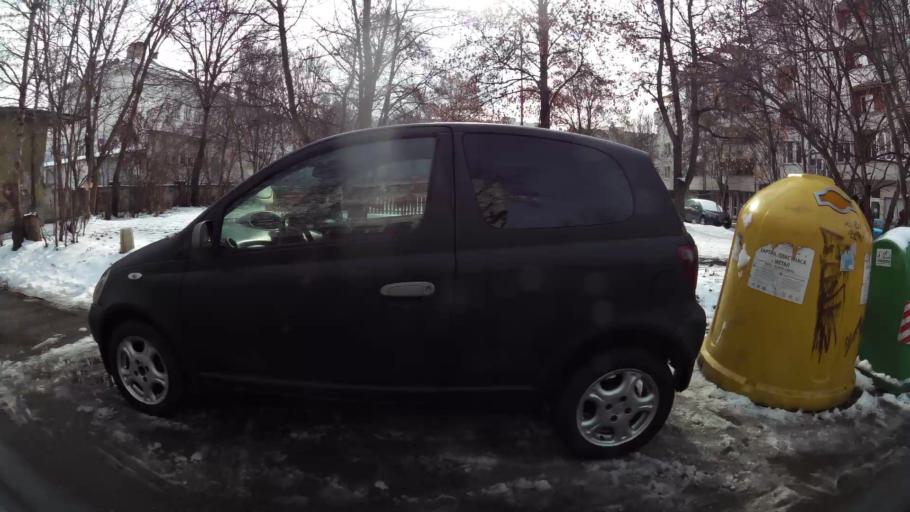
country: BG
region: Sofia-Capital
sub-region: Stolichna Obshtina
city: Sofia
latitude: 42.7068
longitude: 23.3529
